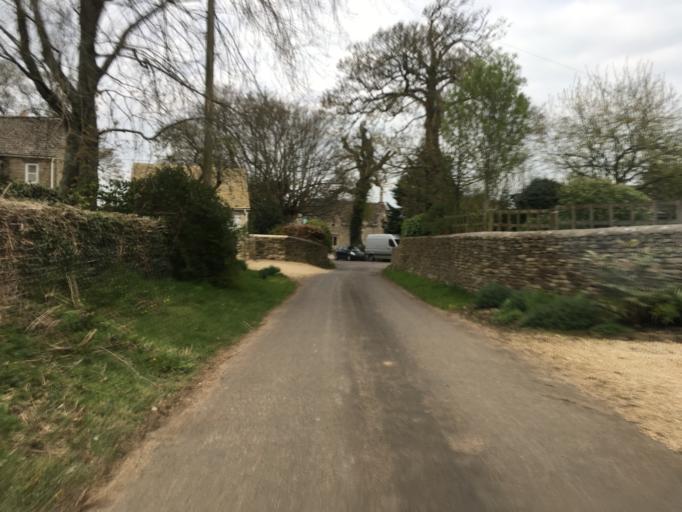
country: GB
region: England
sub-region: Wiltshire
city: Luckington
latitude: 51.6188
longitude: -2.2573
